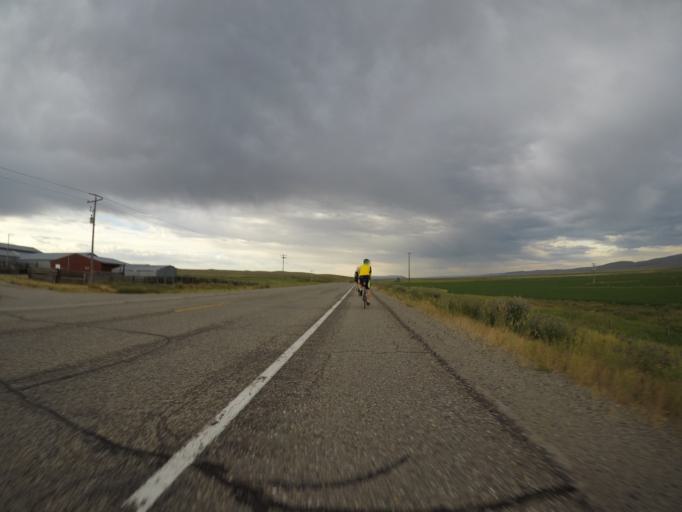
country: US
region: Utah
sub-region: Rich County
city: Randolph
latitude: 41.9779
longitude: -110.9433
